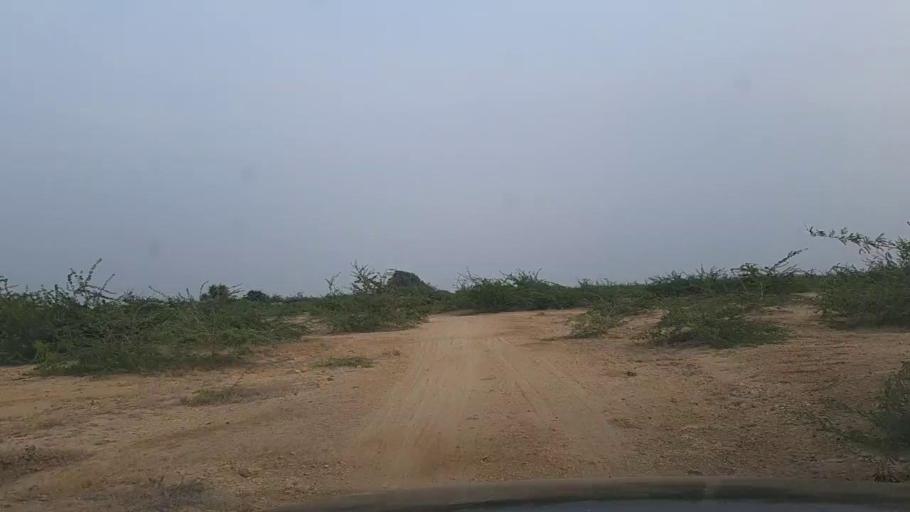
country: PK
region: Sindh
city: Gharo
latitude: 24.7747
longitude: 67.6948
